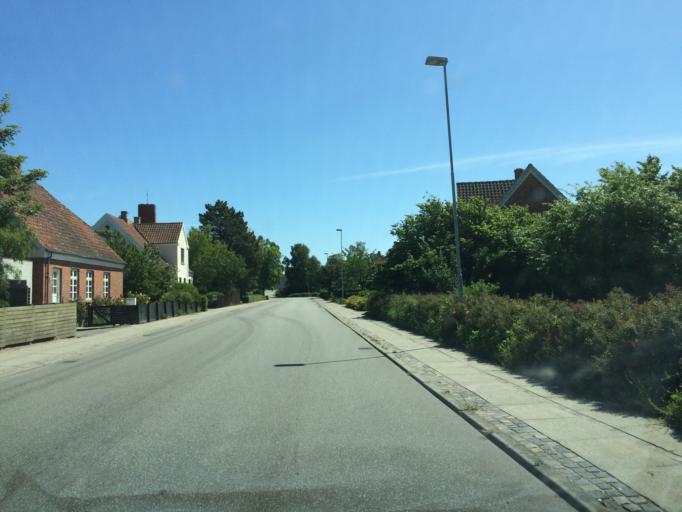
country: DK
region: Central Jutland
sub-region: Samso Kommune
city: Tranebjerg
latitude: 55.8322
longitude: 10.5882
